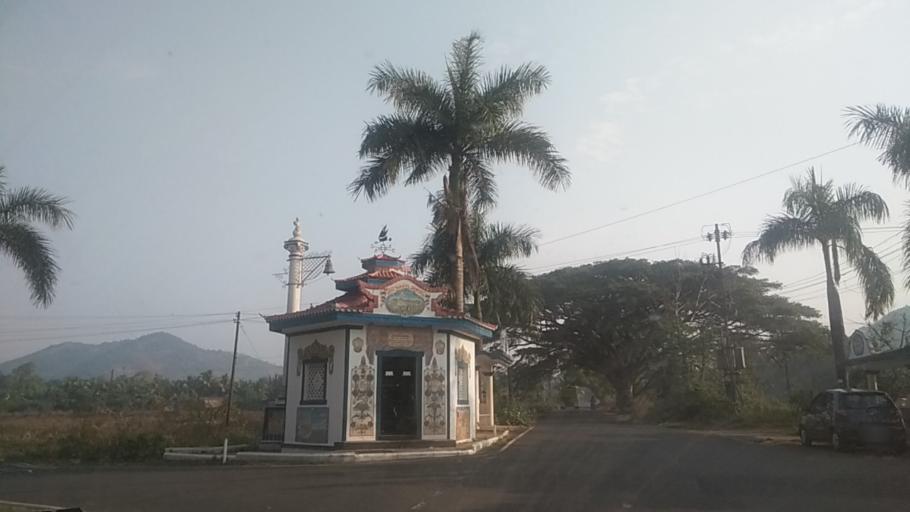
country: IN
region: Goa
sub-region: South Goa
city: Chinchinim
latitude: 15.2198
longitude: 73.9944
